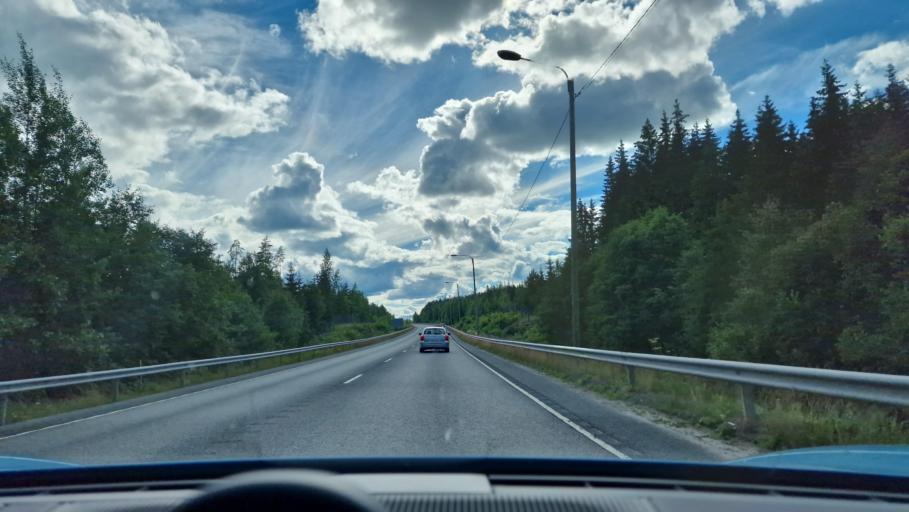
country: FI
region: Pirkanmaa
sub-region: Tampere
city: Orivesi
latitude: 61.6804
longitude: 24.3296
